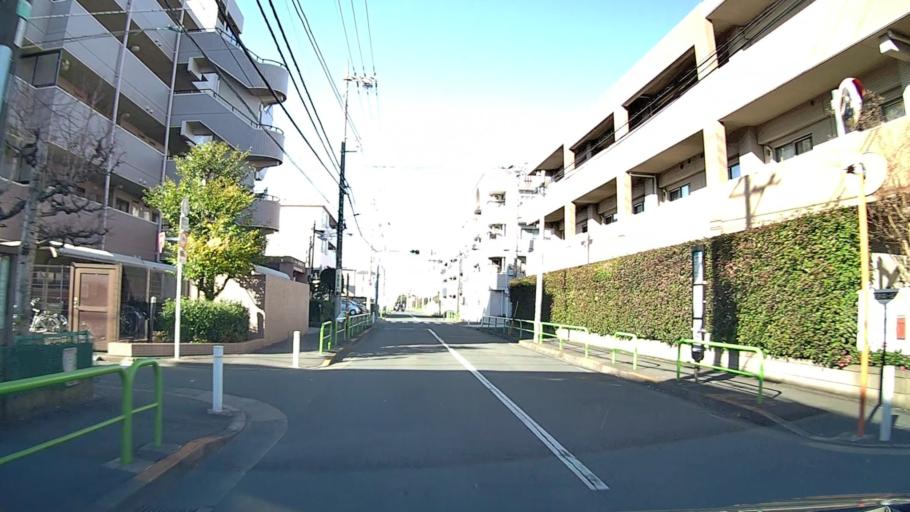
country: JP
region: Saitama
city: Wako
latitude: 35.7526
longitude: 139.6144
